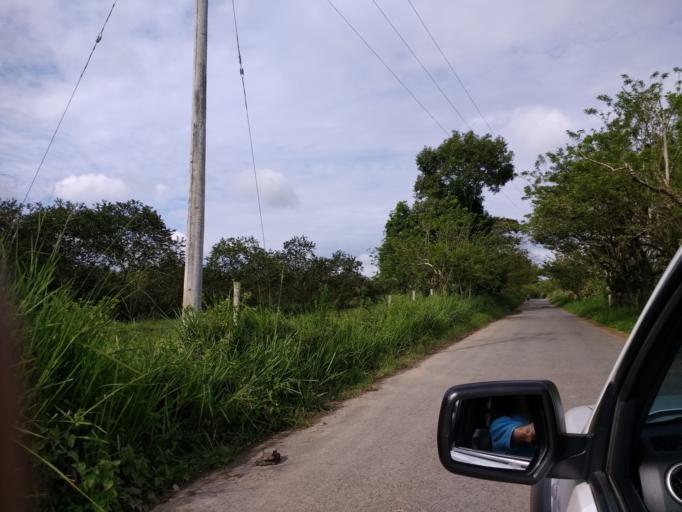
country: CO
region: Quindio
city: Montenegro
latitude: 4.5458
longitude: -75.8276
